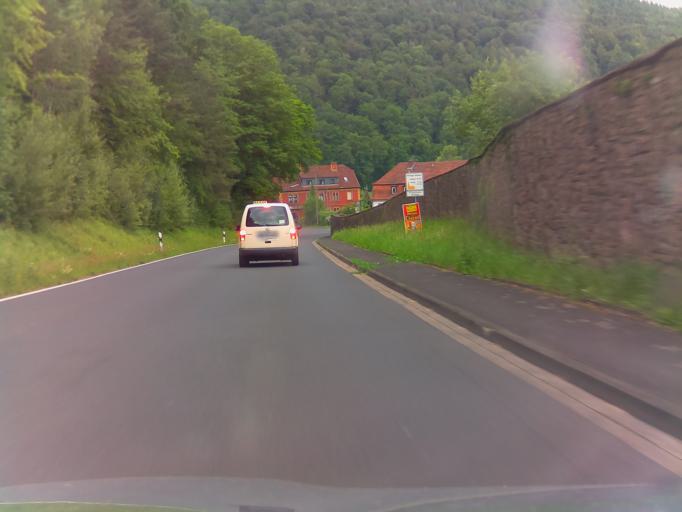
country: DE
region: Bavaria
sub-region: Regierungsbezirk Unterfranken
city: Schonau
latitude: 50.0776
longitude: 9.7212
